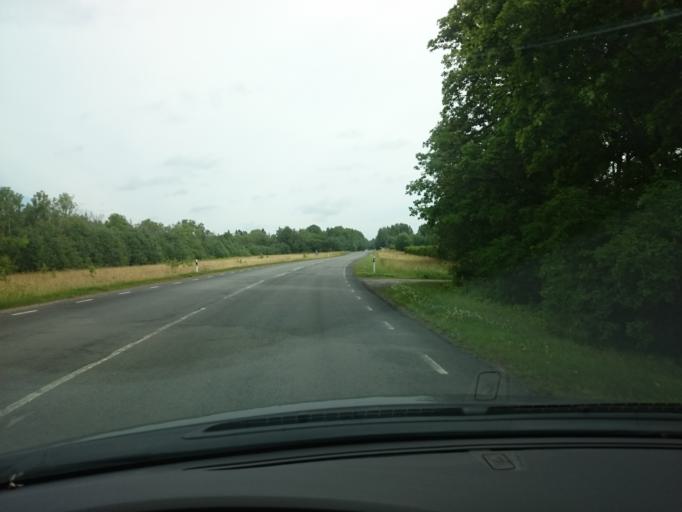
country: EE
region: Laeaene
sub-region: Ridala Parish
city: Uuemoisa
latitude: 58.9739
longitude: 23.6775
